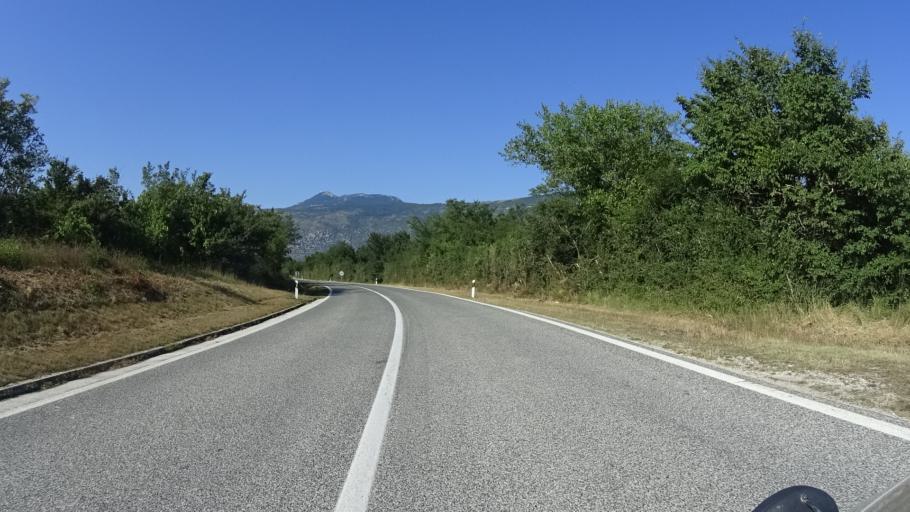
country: HR
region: Istarska
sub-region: Grad Labin
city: Labin
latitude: 45.2067
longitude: 14.1411
